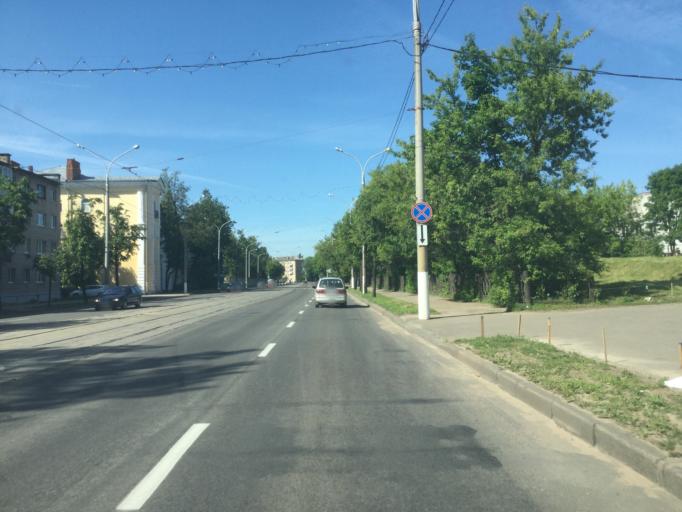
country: BY
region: Vitebsk
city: Vitebsk
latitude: 55.1877
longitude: 30.1893
